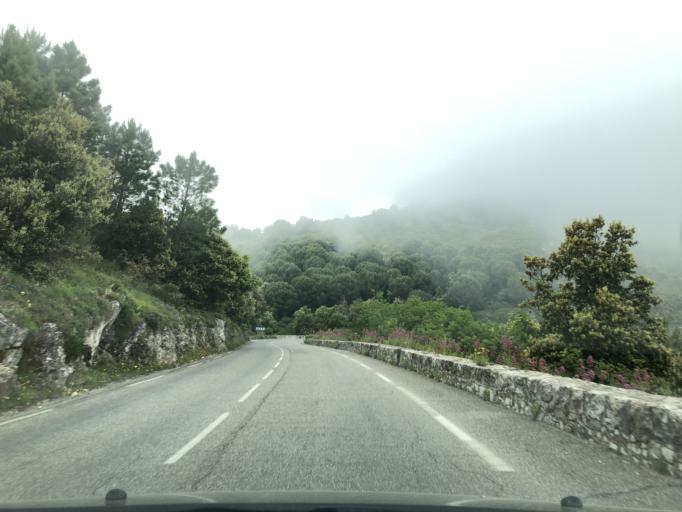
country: FR
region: Provence-Alpes-Cote d'Azur
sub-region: Departement des Alpes-Maritimes
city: Beaulieu-sur-Mer
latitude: 43.7248
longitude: 7.3368
